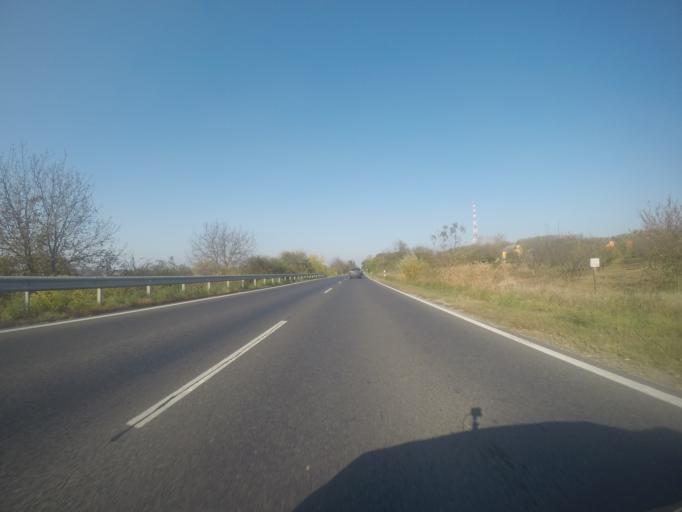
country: HU
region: Tolna
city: Dunafoldvar
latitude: 46.8241
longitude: 18.9065
